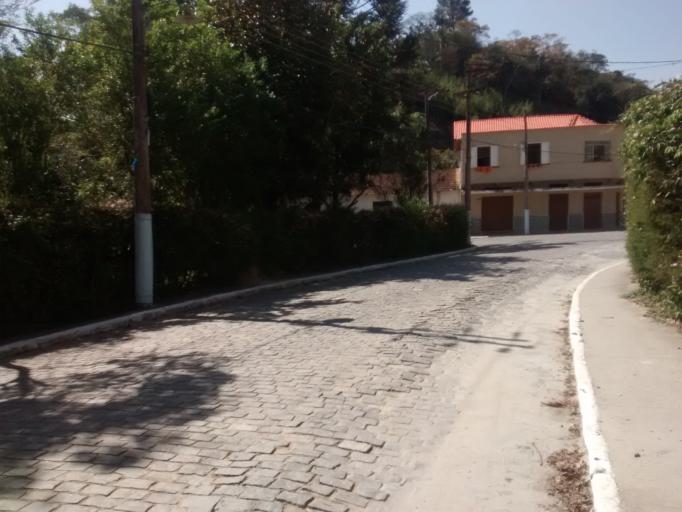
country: BR
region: Rio de Janeiro
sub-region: Vassouras
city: Vassouras
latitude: -22.4740
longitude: -43.5828
